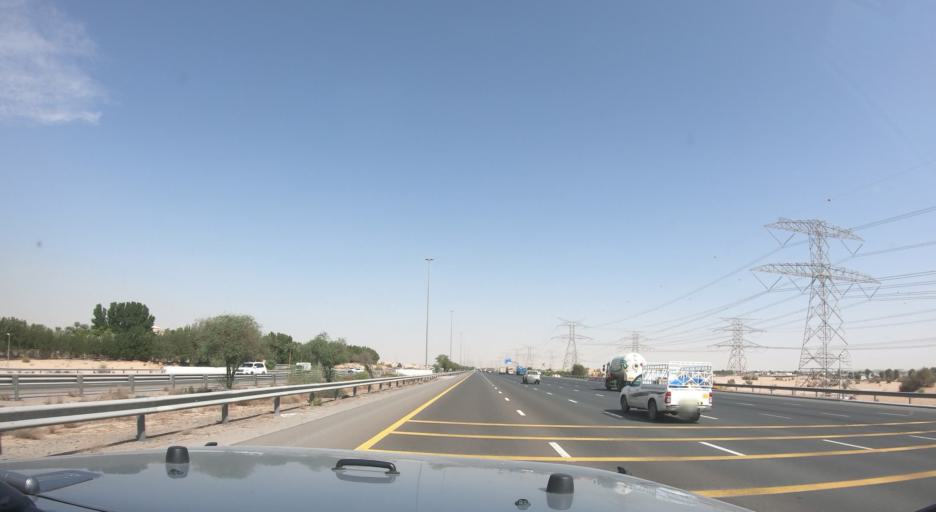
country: AE
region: Ash Shariqah
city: Sharjah
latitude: 25.1871
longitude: 55.5274
